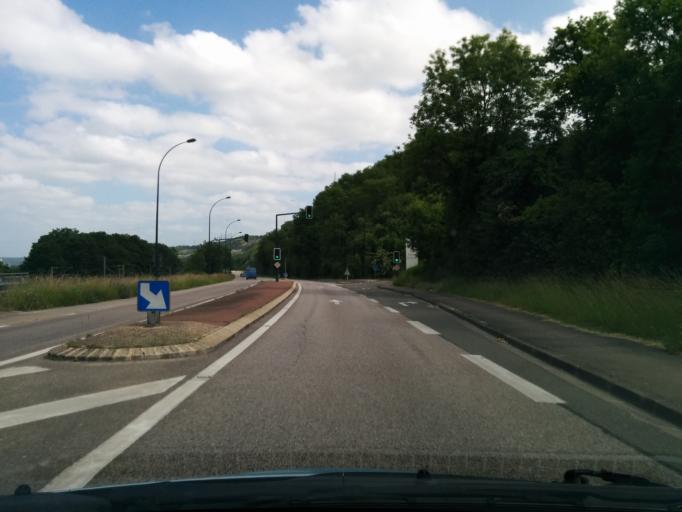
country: FR
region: Ile-de-France
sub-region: Departement des Yvelines
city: Limay
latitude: 48.9711
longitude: 1.7394
